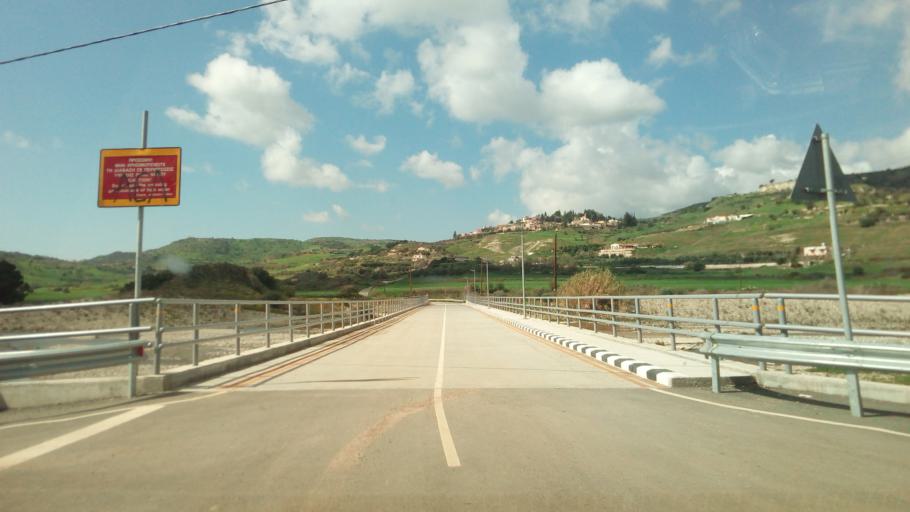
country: CY
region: Pafos
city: Mesogi
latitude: 34.7749
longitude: 32.5823
